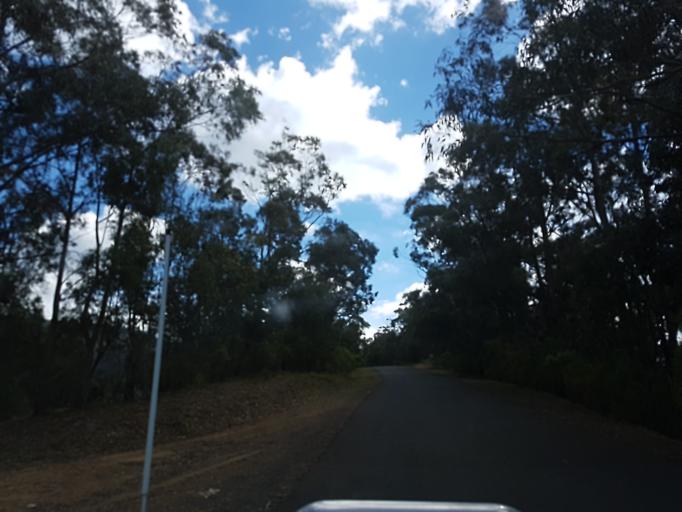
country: AU
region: Victoria
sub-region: East Gippsland
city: Bairnsdale
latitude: -37.4141
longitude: 147.2511
